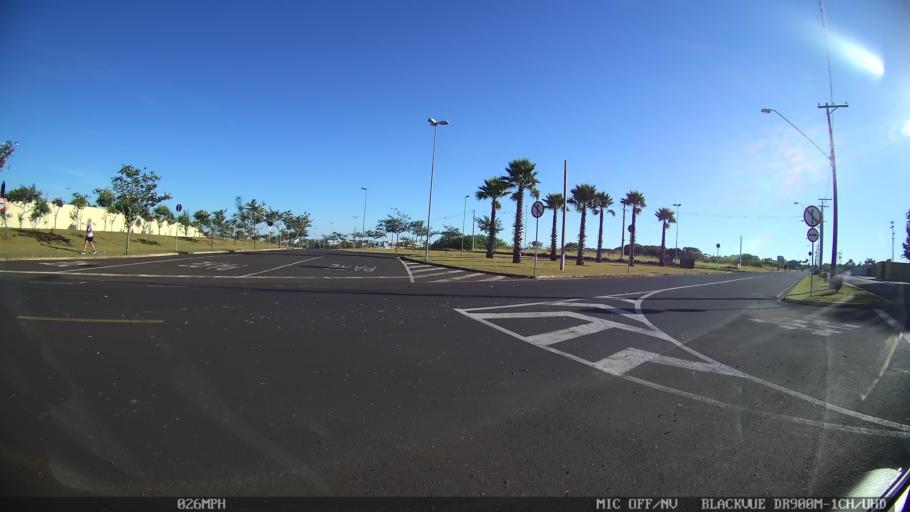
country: BR
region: Sao Paulo
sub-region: Franca
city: Franca
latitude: -20.5770
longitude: -47.4102
